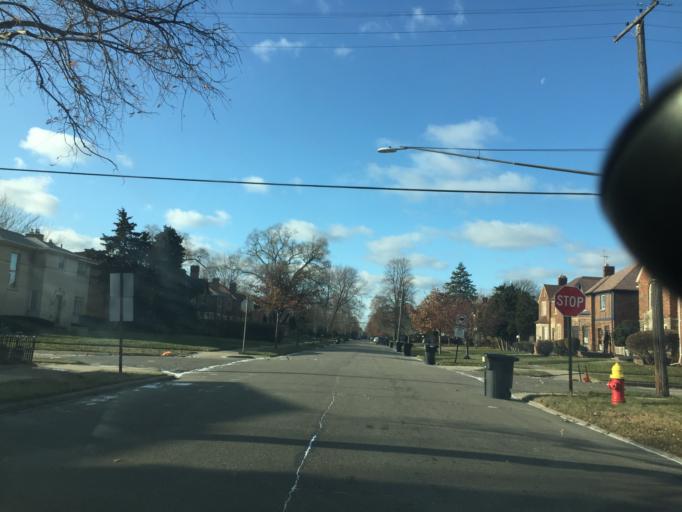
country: US
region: Michigan
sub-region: Wayne County
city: Highland Park
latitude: 42.3851
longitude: -83.1307
